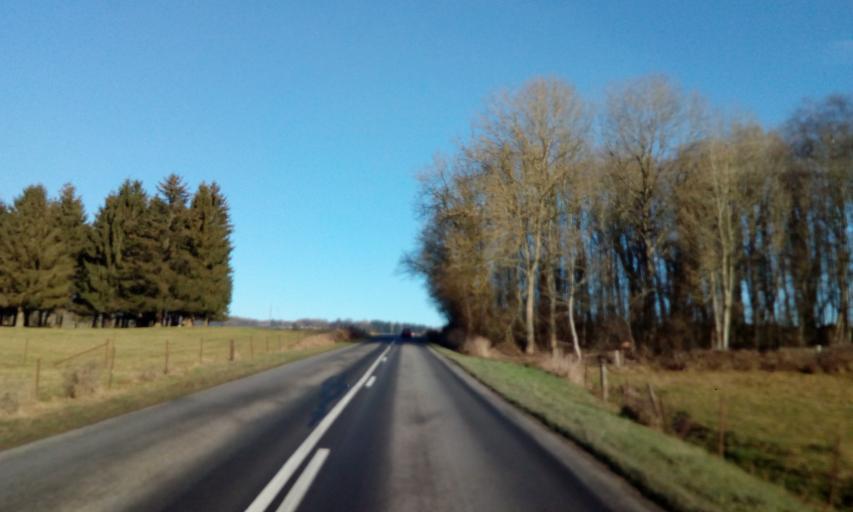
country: FR
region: Champagne-Ardenne
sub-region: Departement des Ardennes
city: Rimogne
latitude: 49.8372
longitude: 4.5044
